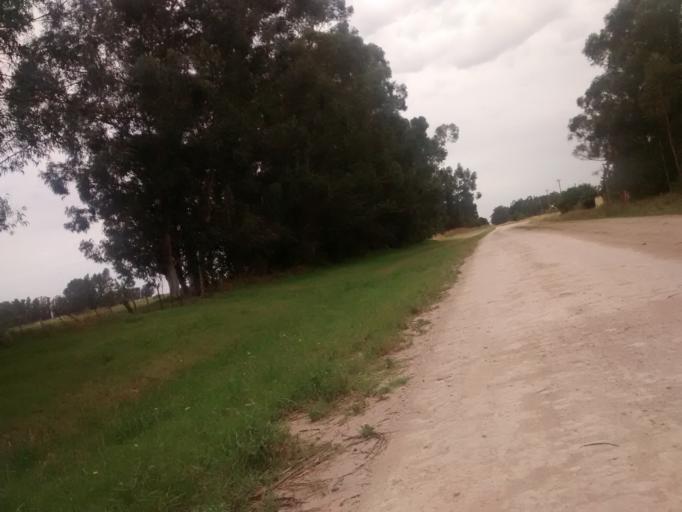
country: AR
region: Buenos Aires
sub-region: Partido de Loberia
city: Loberia
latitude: -38.1940
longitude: -58.7406
